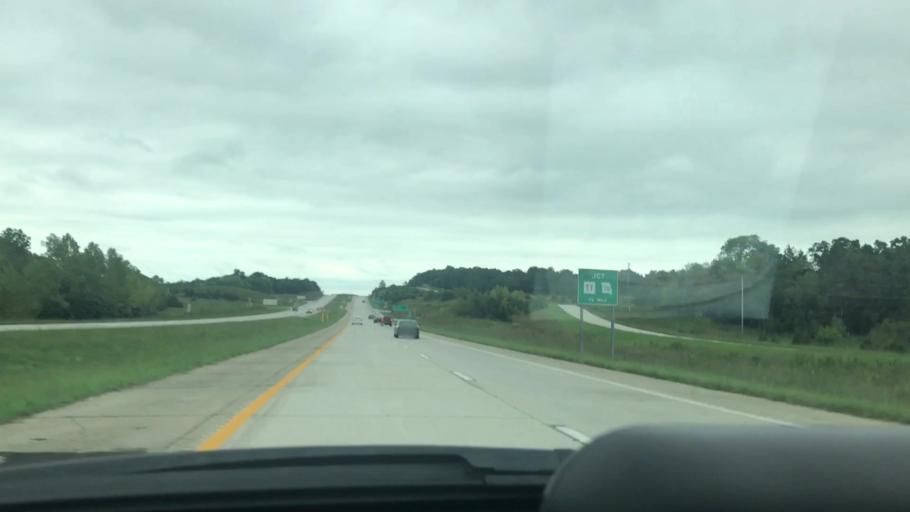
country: US
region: Missouri
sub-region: Greene County
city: Fair Grove
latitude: 37.5135
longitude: -93.1386
